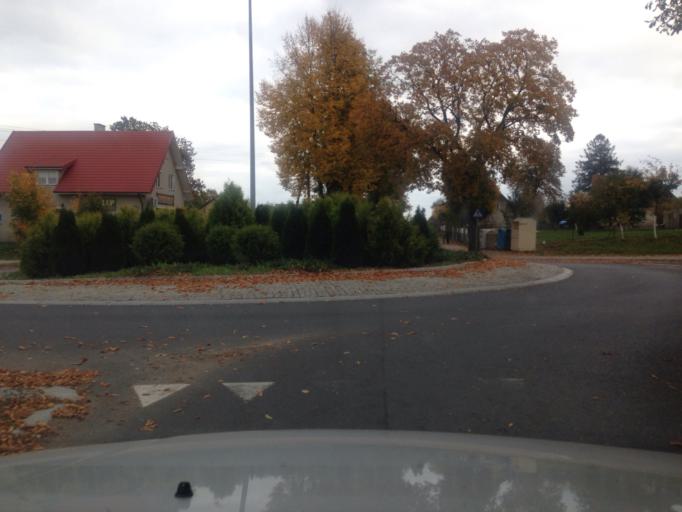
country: PL
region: Warmian-Masurian Voivodeship
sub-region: Powiat ostrodzki
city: Gierzwald
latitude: 53.4960
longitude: 20.1343
